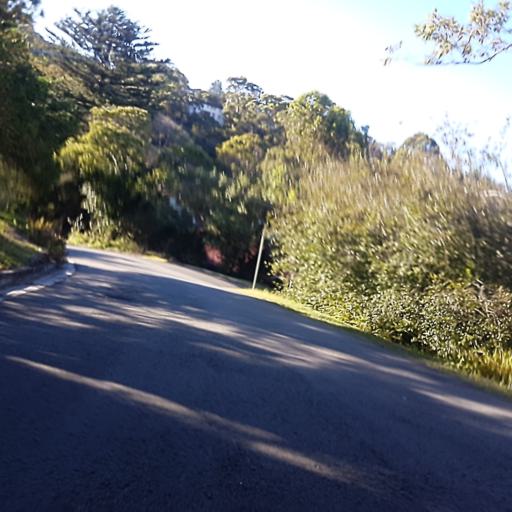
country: AU
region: New South Wales
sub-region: Ku-ring-gai
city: Roseville Chase
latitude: -33.7775
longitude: 151.2042
